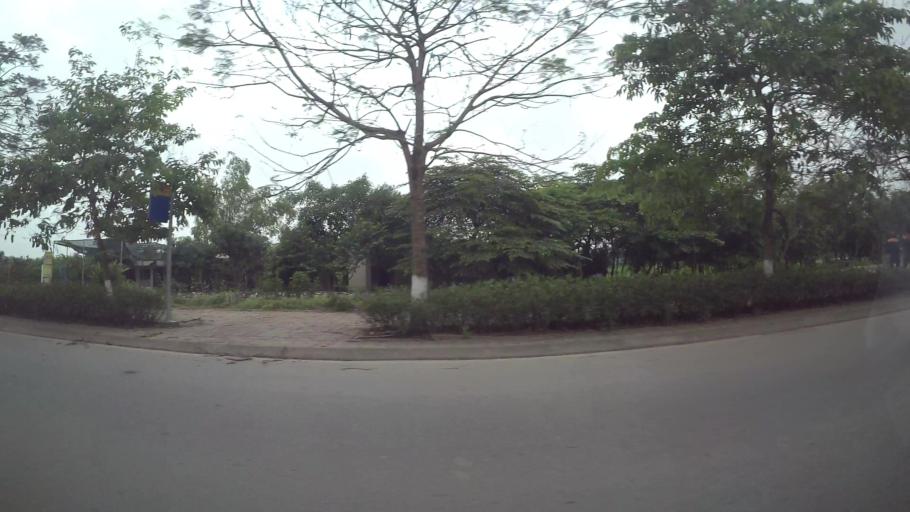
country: VN
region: Ha Noi
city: Trau Quy
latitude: 21.0502
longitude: 105.9218
